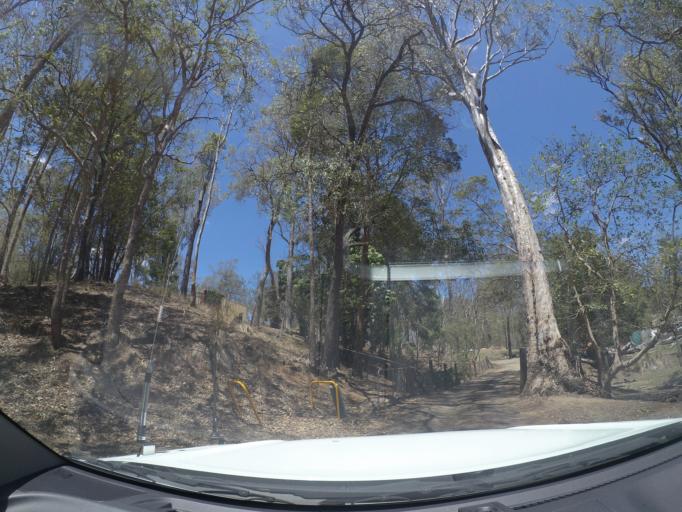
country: AU
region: Queensland
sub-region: Ipswich
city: Deebing Heights
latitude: -27.7688
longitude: 152.8117
